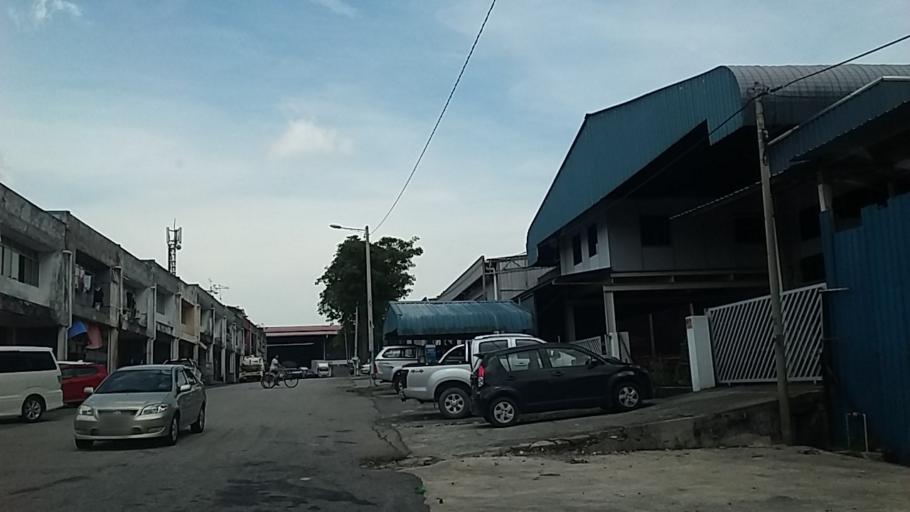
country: MY
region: Johor
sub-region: Daerah Batu Pahat
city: Batu Pahat
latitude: 1.7865
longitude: 102.9683
